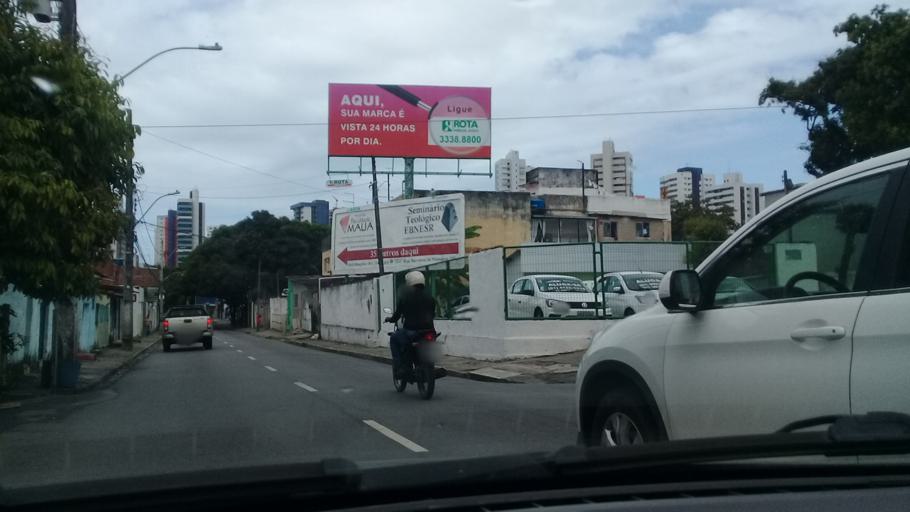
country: BR
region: Pernambuco
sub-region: Recife
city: Recife
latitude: -8.1356
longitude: -34.9100
